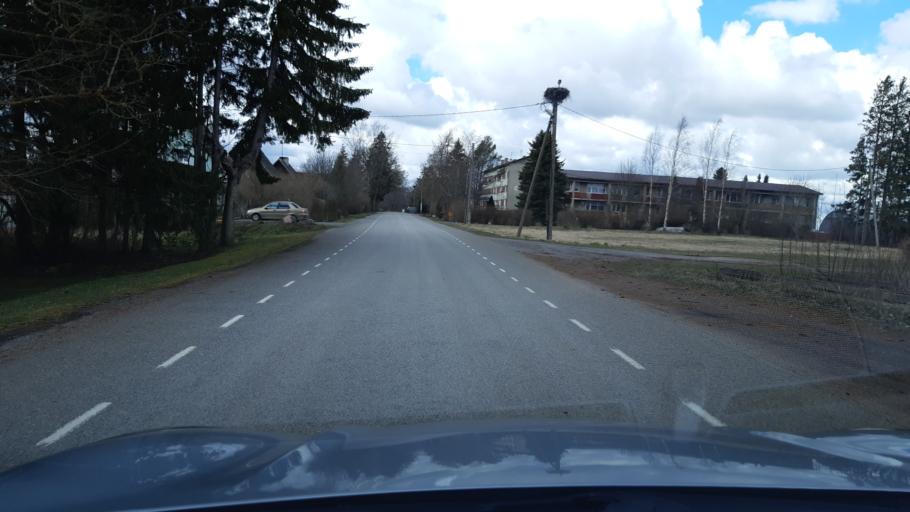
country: EE
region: Raplamaa
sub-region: Kehtna vald
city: Kehtna
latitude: 59.0407
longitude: 25.1258
